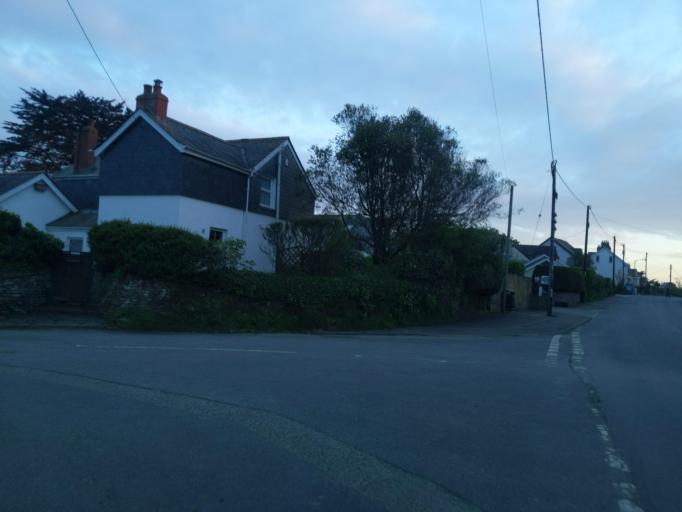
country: GB
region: England
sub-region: Cornwall
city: Polzeath
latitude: 50.5505
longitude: -4.9017
